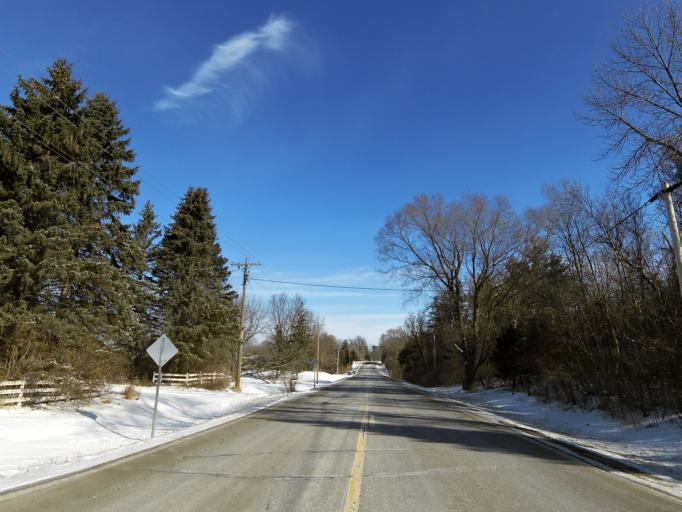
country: US
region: Minnesota
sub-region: Washington County
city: Cottage Grove
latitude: 44.7475
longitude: -92.9361
